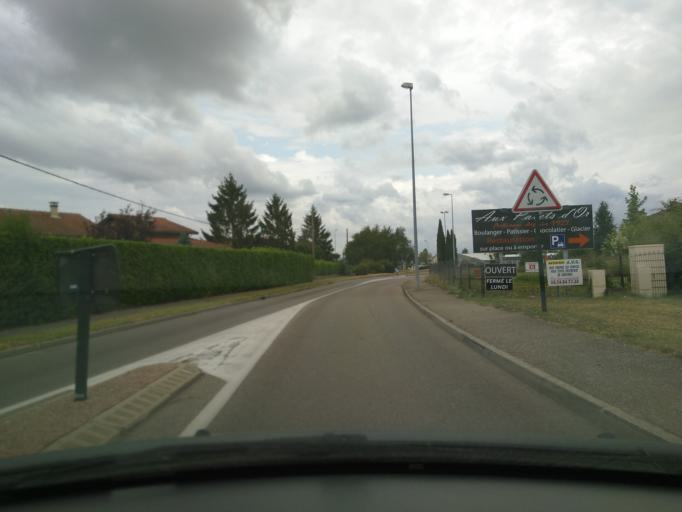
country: FR
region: Rhone-Alpes
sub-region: Departement de l'Isere
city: Beaurepaire
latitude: 45.3475
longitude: 5.0410
